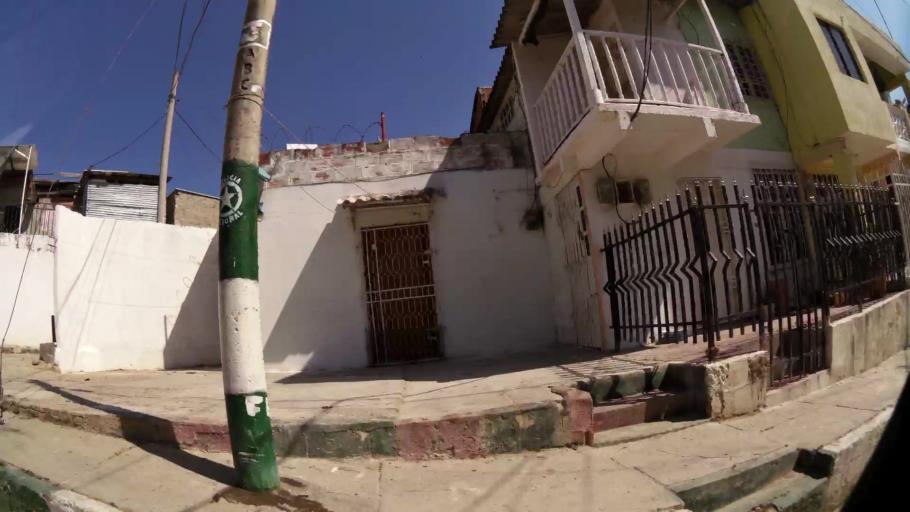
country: CO
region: Bolivar
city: Cartagena
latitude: 10.3953
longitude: -75.5083
